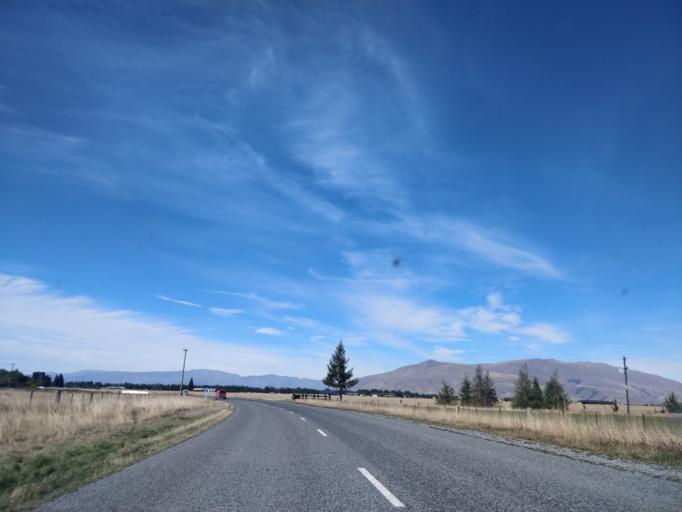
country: NZ
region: Otago
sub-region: Queenstown-Lakes District
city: Wanaka
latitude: -44.2343
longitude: 170.0705
